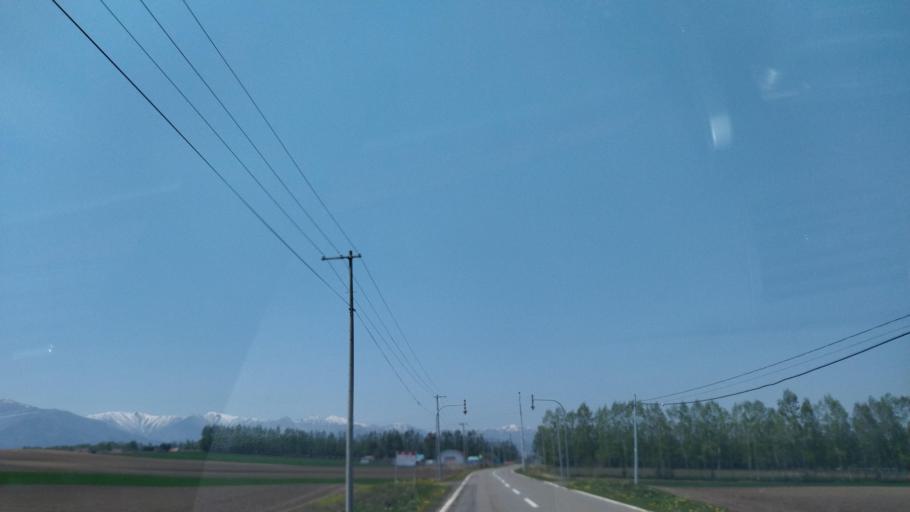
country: JP
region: Hokkaido
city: Obihiro
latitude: 42.9048
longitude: 143.0000
